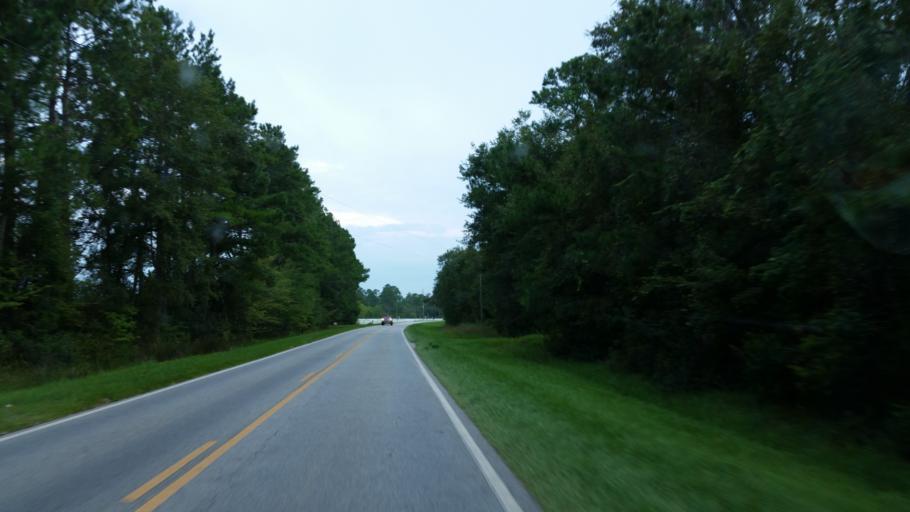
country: US
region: Georgia
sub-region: Lowndes County
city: Valdosta
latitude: 30.7603
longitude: -83.3044
